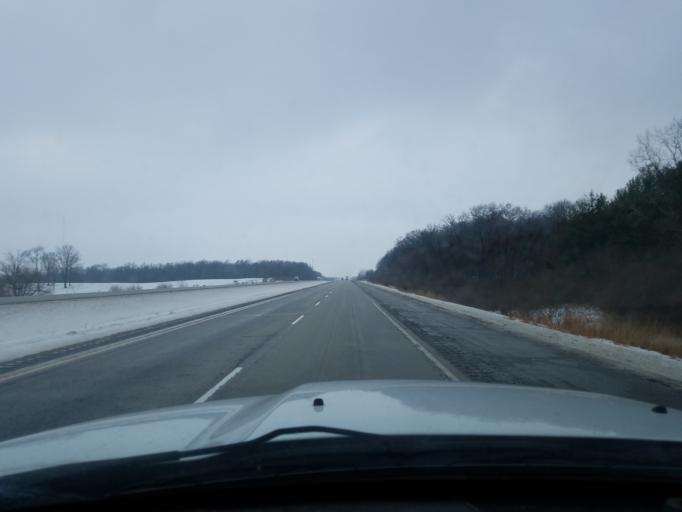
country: US
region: Indiana
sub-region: Fulton County
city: Rochester
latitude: 41.1254
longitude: -86.2396
